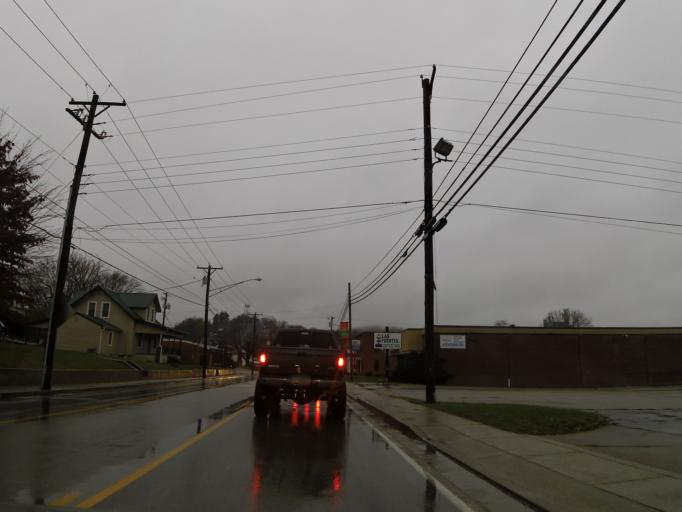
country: US
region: Kentucky
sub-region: Rockcastle County
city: Mount Vernon
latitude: 37.3571
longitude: -84.3395
